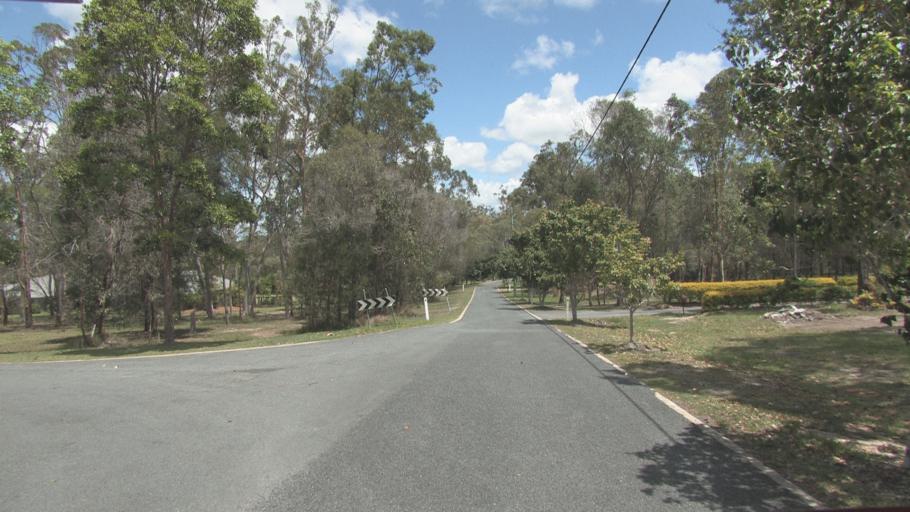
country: AU
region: Queensland
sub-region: Logan
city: Beenleigh
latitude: -27.6595
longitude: 153.2301
